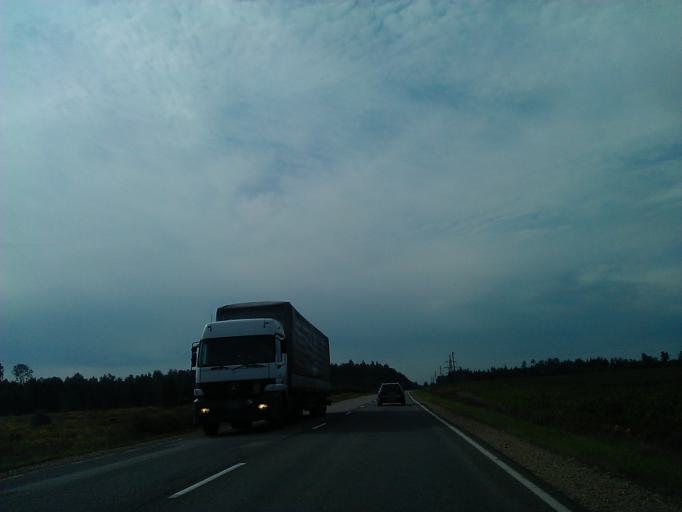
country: LV
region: Salaspils
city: Salaspils
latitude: 56.8816
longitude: 24.4077
